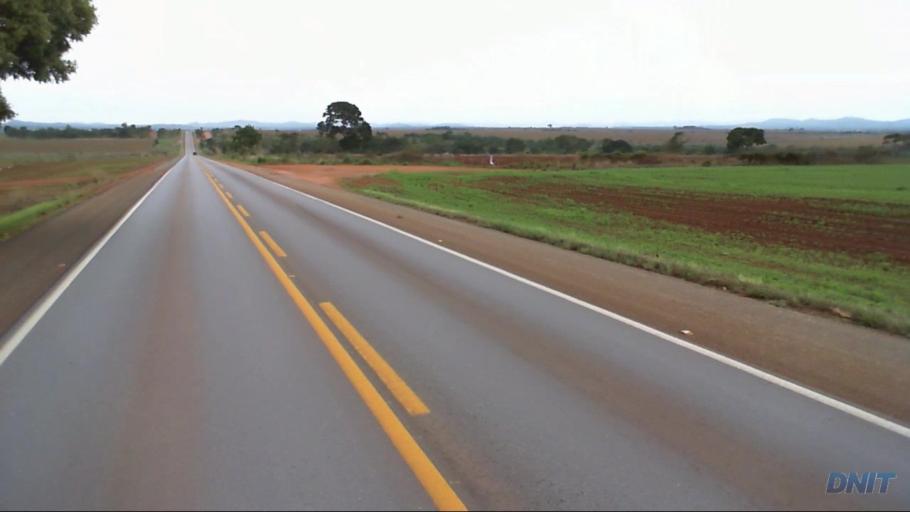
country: BR
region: Goias
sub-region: Uruacu
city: Uruacu
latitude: -14.6611
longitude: -49.1538
